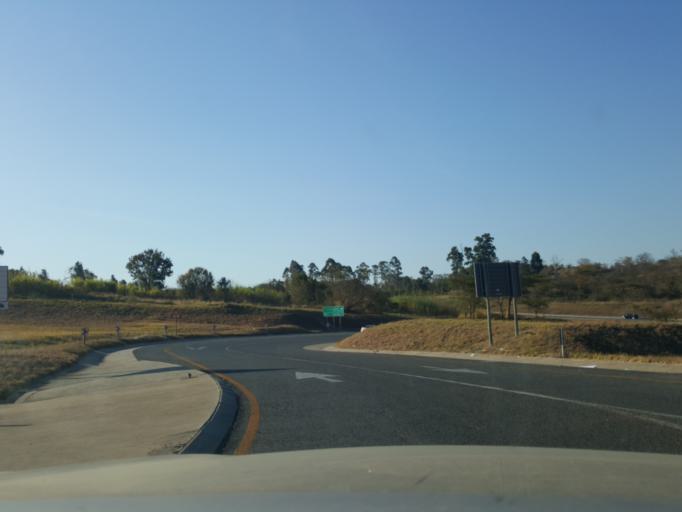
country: ZA
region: Mpumalanga
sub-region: Ehlanzeni District
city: Nelspruit
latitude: -25.4380
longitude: 30.9494
